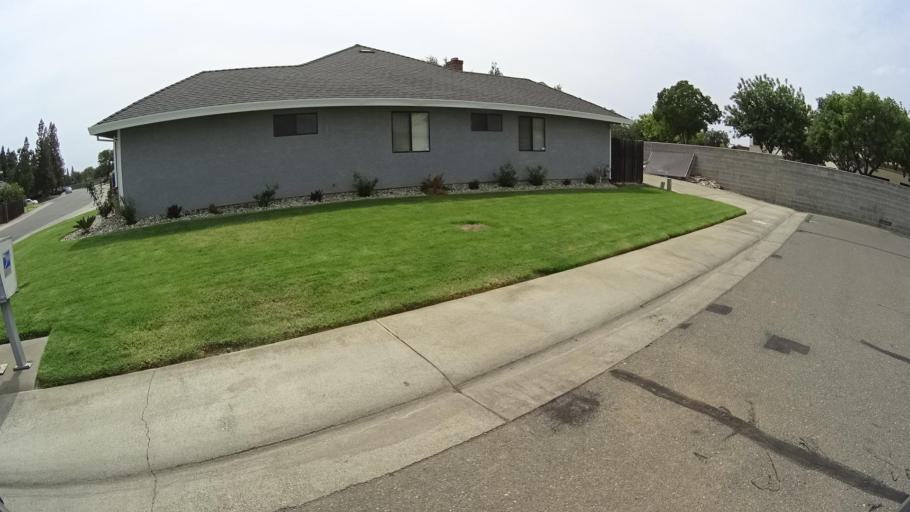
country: US
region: California
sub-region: Sacramento County
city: Elk Grove
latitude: 38.4158
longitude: -121.3898
